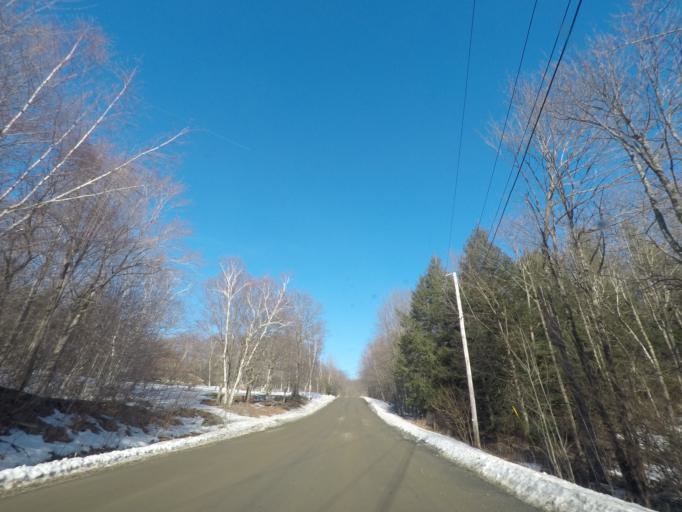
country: US
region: New York
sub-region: Rensselaer County
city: Averill Park
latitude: 42.6419
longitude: -73.5093
